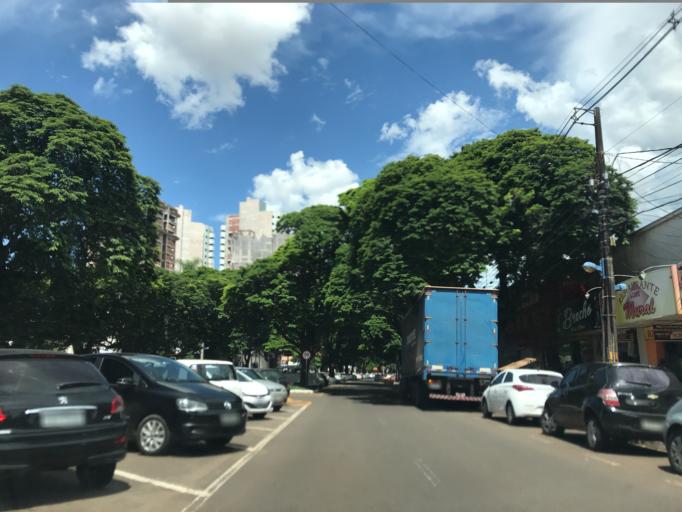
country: BR
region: Parana
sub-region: Maringa
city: Maringa
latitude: -23.4200
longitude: -51.9307
